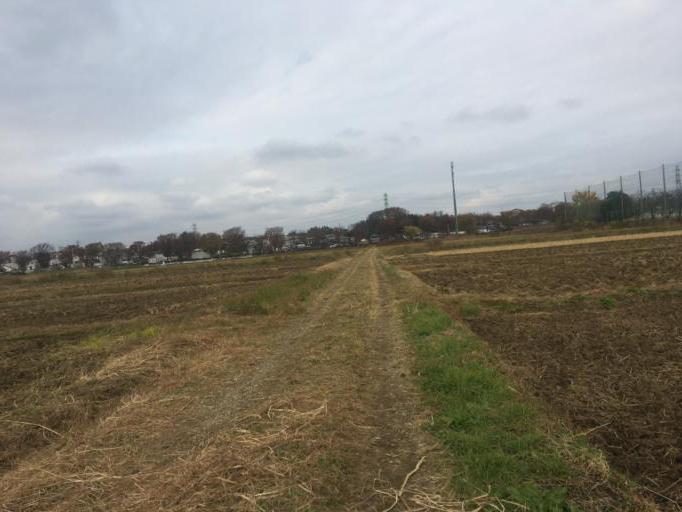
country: JP
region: Saitama
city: Shiki
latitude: 35.8377
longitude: 139.5692
